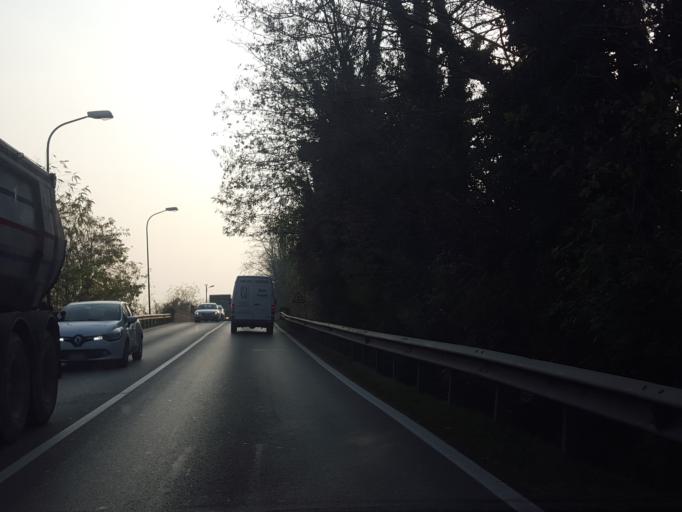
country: IT
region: Veneto
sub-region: Provincia di Treviso
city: Treviso
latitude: 45.6646
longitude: 12.2222
